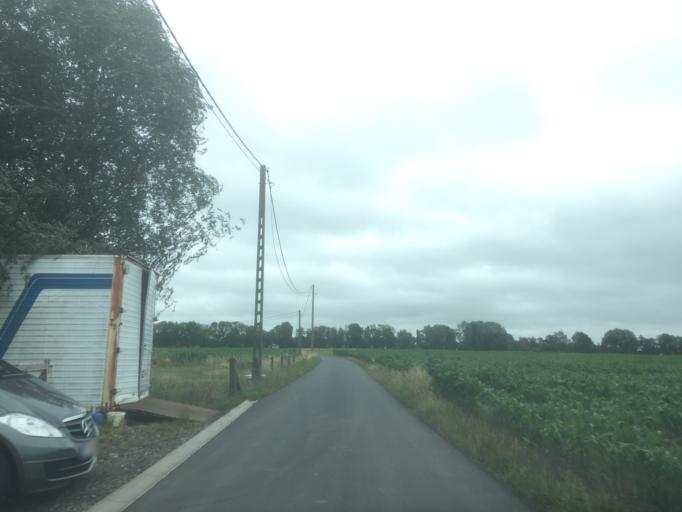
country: BE
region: Flanders
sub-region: Provincie West-Vlaanderen
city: Roeselare
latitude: 50.9289
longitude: 3.1010
